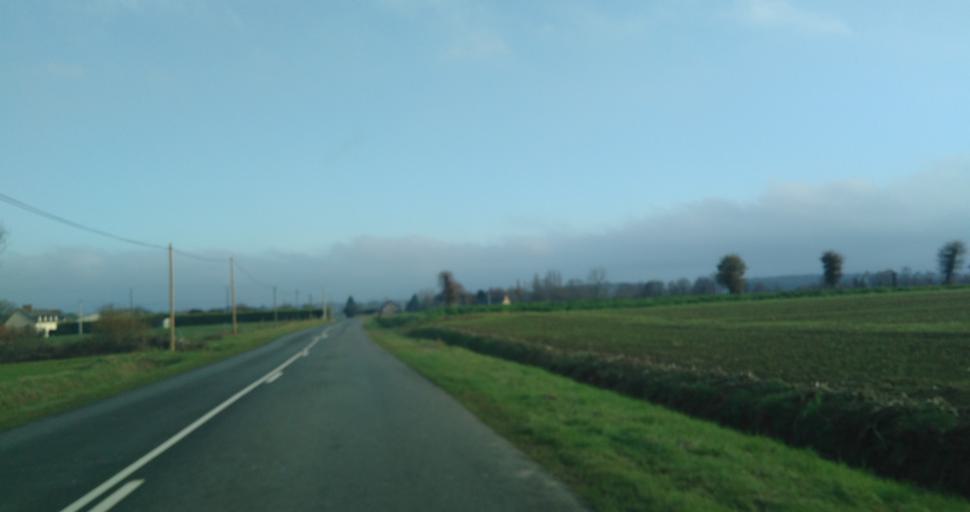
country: FR
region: Brittany
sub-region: Departement d'Ille-et-Vilaine
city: Saint-Meen-le-Grand
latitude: 48.1785
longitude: -2.1456
